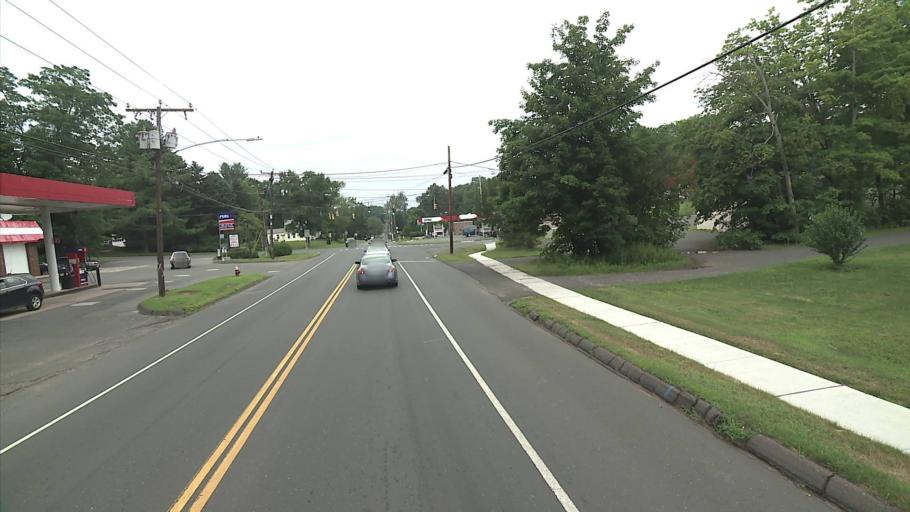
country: US
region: Connecticut
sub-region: Middlesex County
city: Cromwell
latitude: 41.6535
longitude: -72.6409
